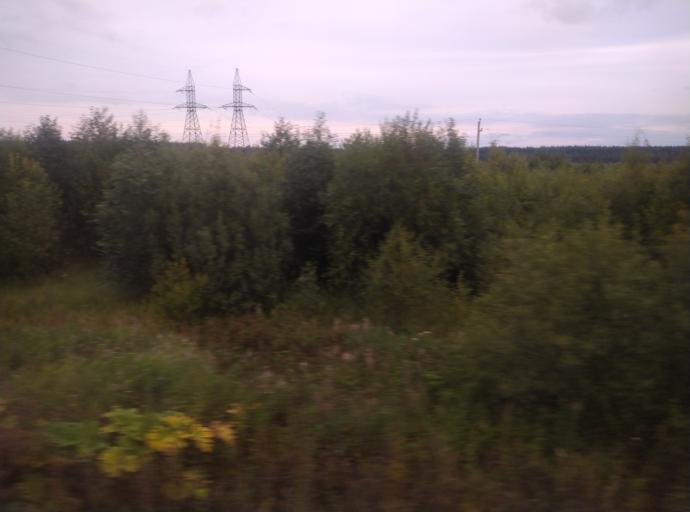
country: RU
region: Jaroslavl
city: Tunoshna
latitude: 57.4855
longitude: 40.1574
